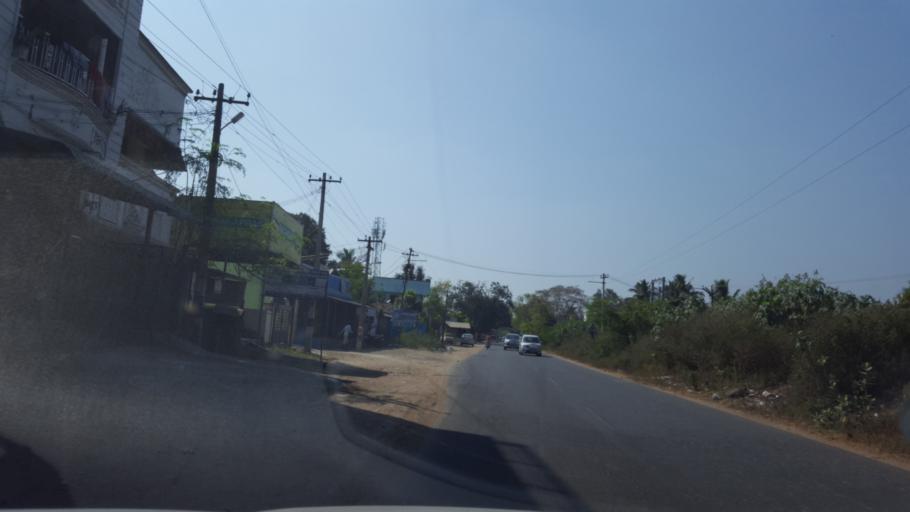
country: IN
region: Tamil Nadu
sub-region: Kancheepuram
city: Kanchipuram
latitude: 12.8575
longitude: 79.6816
